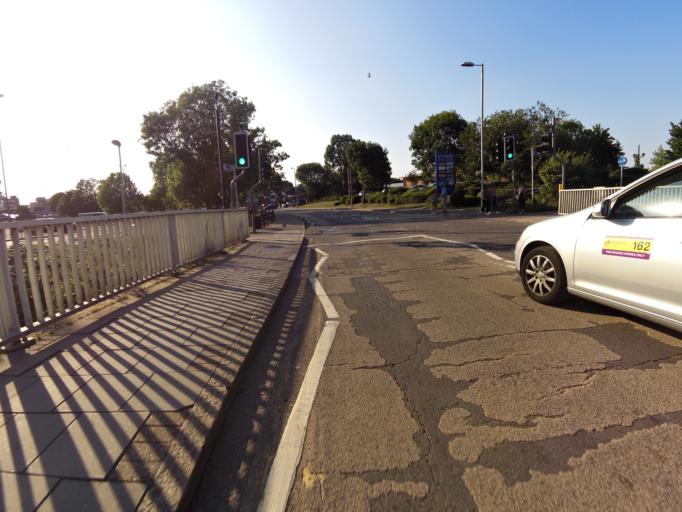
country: GB
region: England
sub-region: Essex
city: Chelmsford
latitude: 51.7363
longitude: 0.4791
